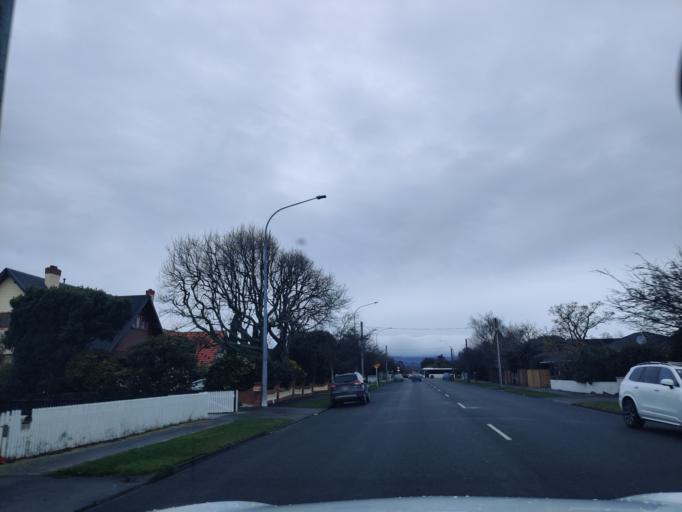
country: NZ
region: Manawatu-Wanganui
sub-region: Palmerston North City
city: Palmerston North
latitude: -40.3438
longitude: 175.6157
